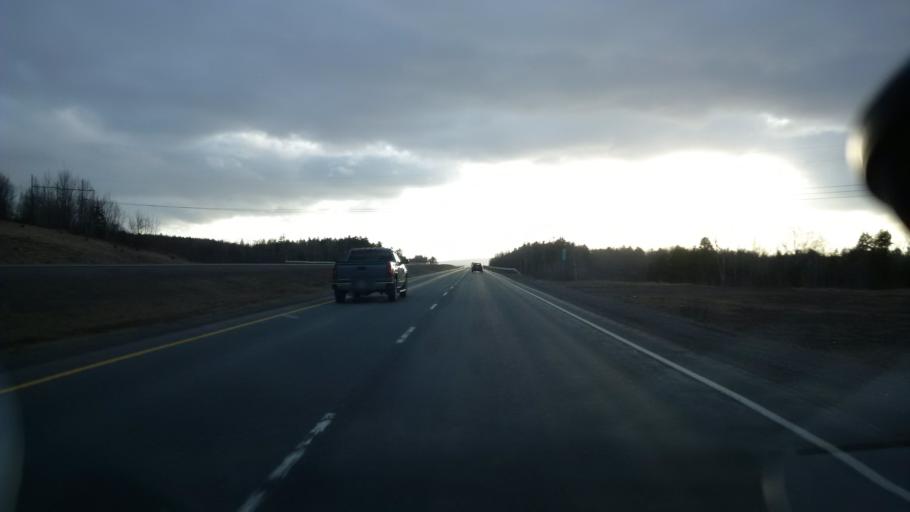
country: CA
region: Nova Scotia
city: Pictou
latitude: 45.5440
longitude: -62.8340
